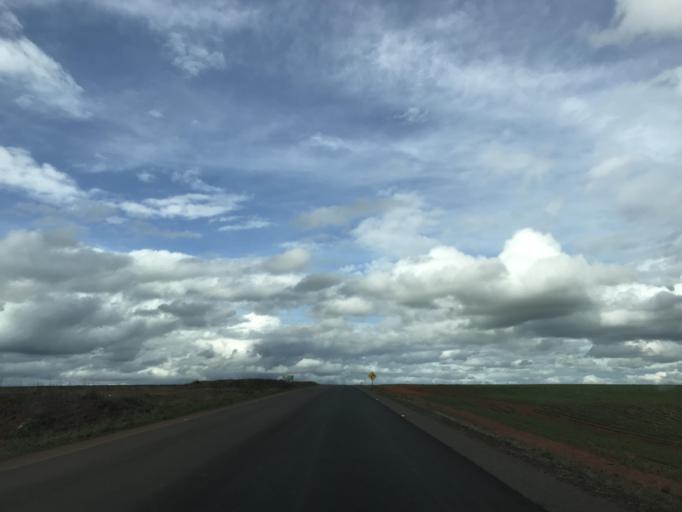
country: BR
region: Goias
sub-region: Vianopolis
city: Vianopolis
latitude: -16.9750
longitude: -48.6612
